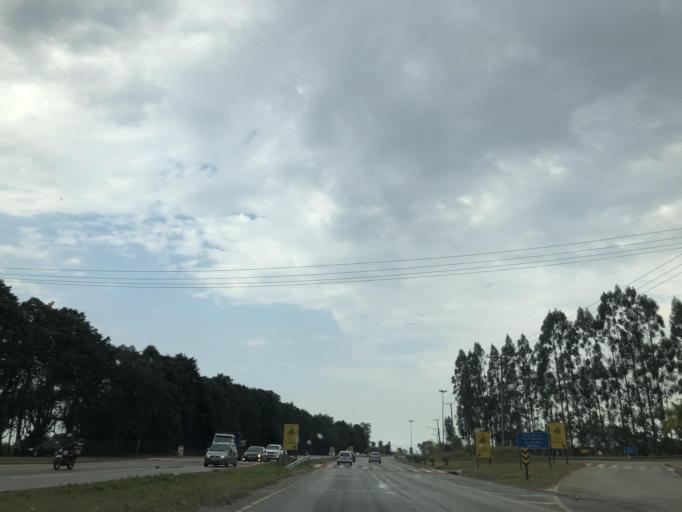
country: BR
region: Sao Paulo
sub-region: Salto De Pirapora
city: Salto de Pirapora
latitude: -23.5798
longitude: -47.5257
